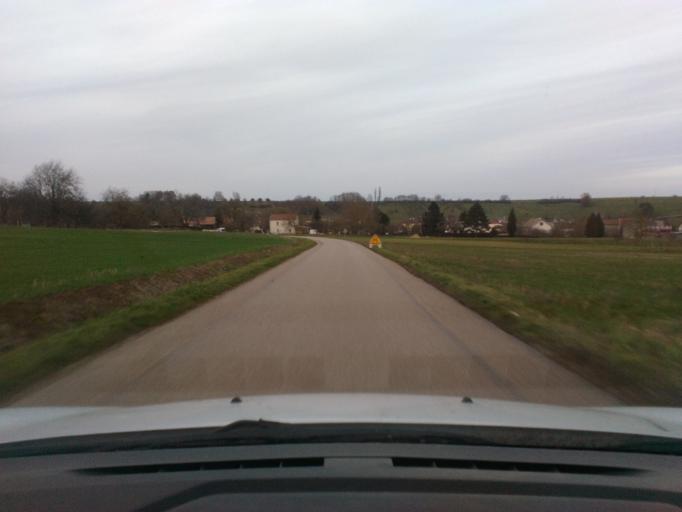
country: FR
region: Lorraine
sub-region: Departement des Vosges
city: Mirecourt
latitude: 48.3069
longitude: 6.0987
